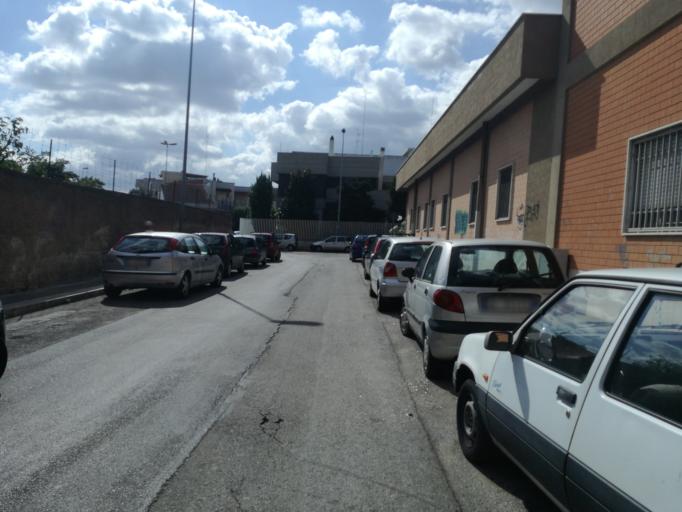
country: IT
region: Apulia
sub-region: Provincia di Bari
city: Triggiano
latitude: 41.0657
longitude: 16.9285
